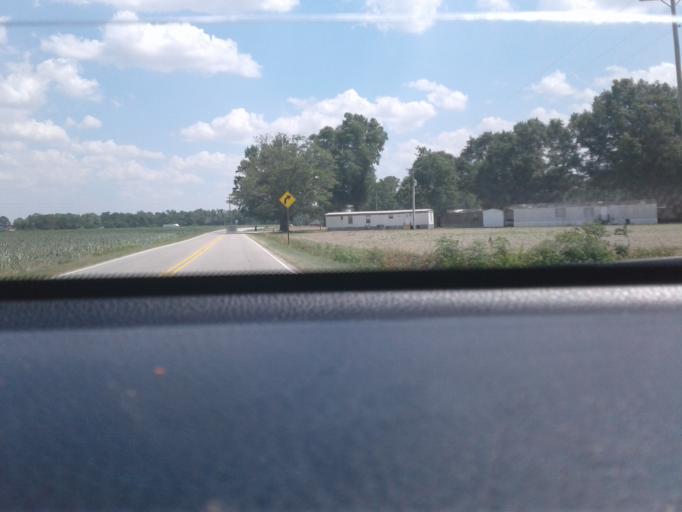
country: US
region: North Carolina
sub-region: Harnett County
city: Erwin
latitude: 35.2959
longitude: -78.6659
